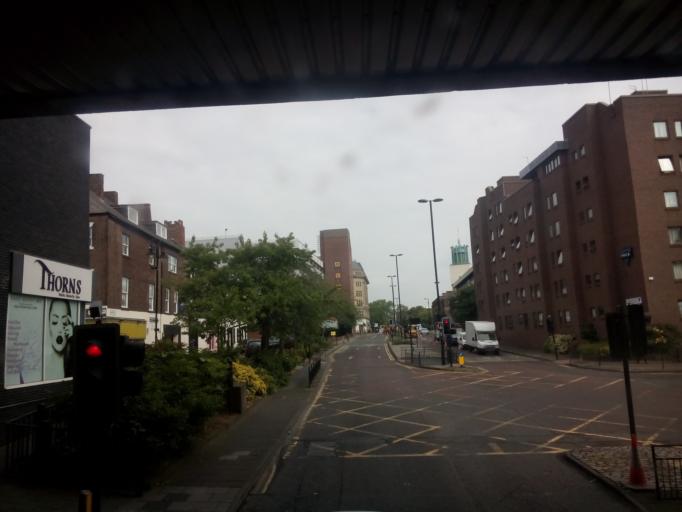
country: GB
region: England
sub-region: Newcastle upon Tyne
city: Newcastle upon Tyne
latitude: 54.9758
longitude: -1.6103
